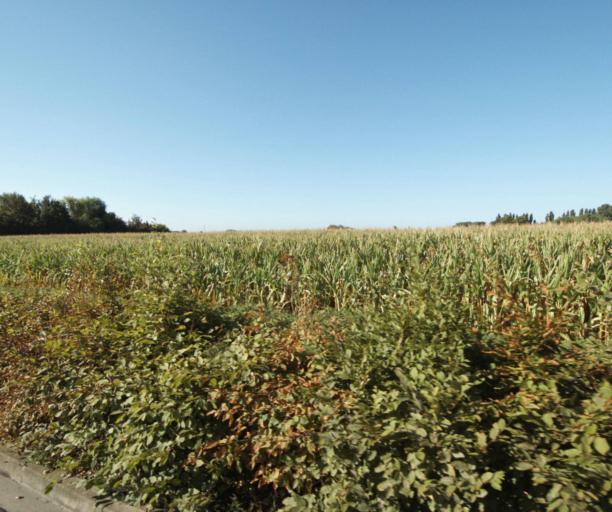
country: FR
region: Nord-Pas-de-Calais
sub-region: Departement du Nord
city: Toufflers
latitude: 50.6561
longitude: 3.2427
